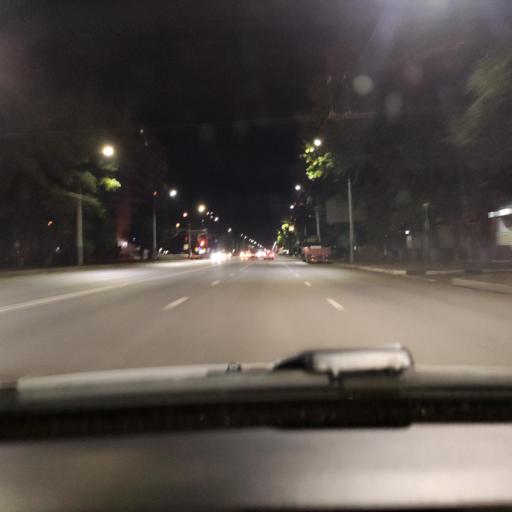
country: RU
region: Voronezj
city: Voronezh
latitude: 51.6455
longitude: 39.2388
